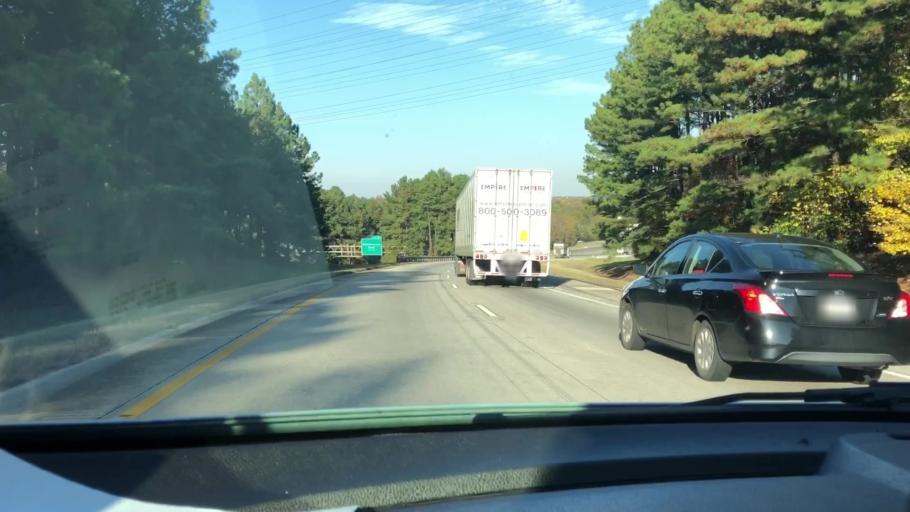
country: US
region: Georgia
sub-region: Clayton County
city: Conley
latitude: 33.6731
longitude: -84.3251
